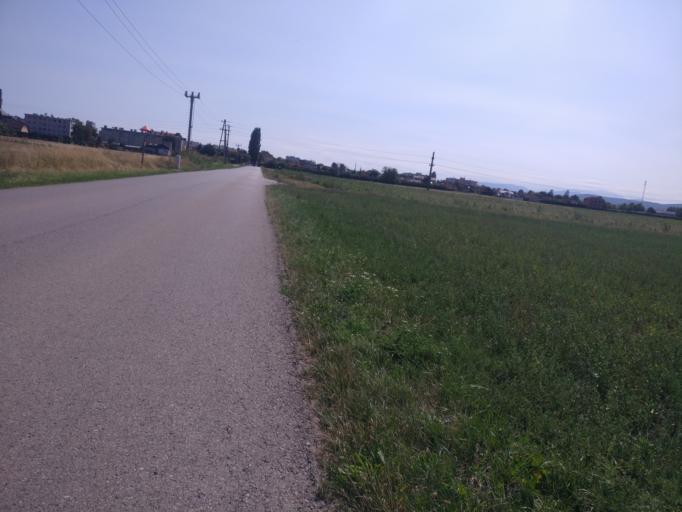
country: AT
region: Lower Austria
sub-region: Politischer Bezirk Modling
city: Guntramsdorf
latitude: 48.0332
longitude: 16.3079
